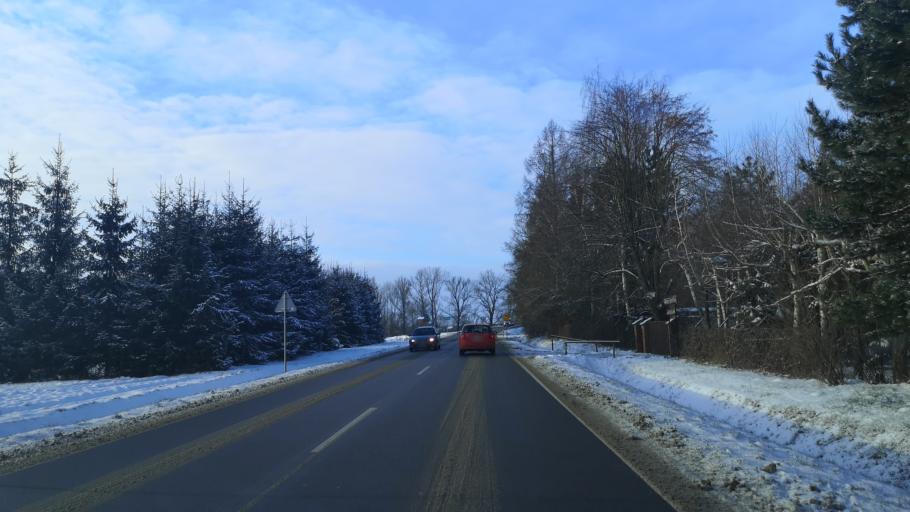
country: PL
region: Subcarpathian Voivodeship
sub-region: Powiat przeworski
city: Sieniawa
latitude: 50.1680
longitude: 22.5899
